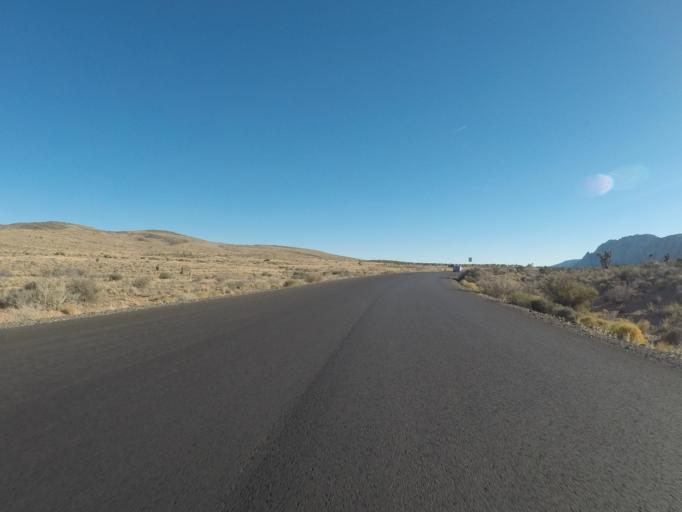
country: US
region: Nevada
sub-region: Clark County
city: Summerlin South
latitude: 36.1143
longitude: -115.4506
